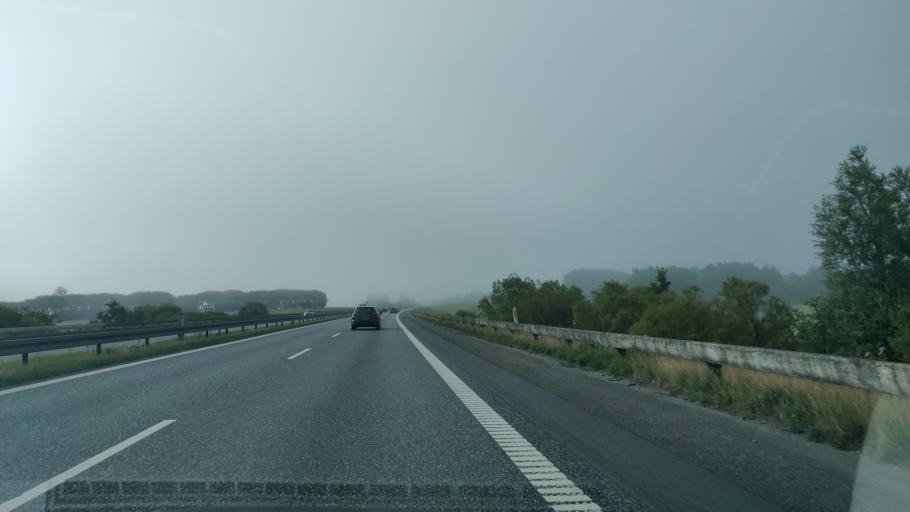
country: DK
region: Central Jutland
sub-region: Randers Kommune
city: Spentrup
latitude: 56.5164
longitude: 9.9621
